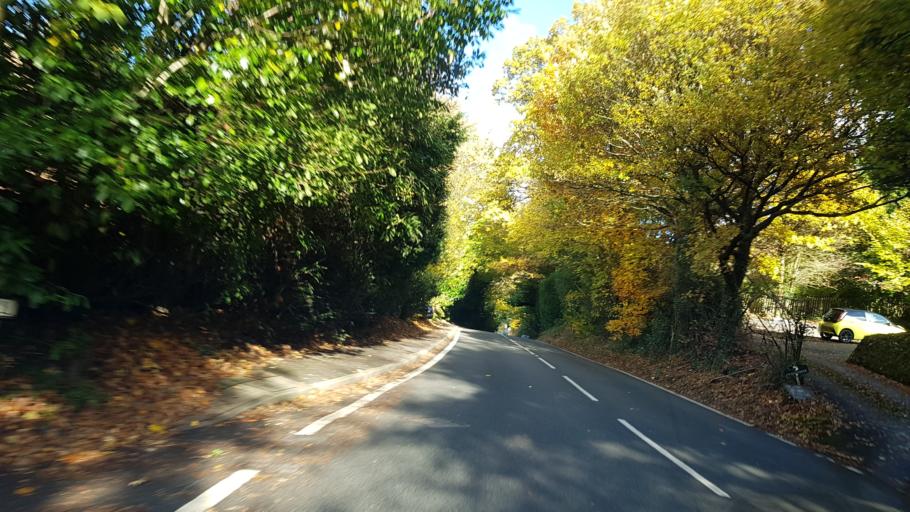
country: GB
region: England
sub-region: Surrey
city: Hindhead
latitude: 51.0907
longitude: -0.7414
